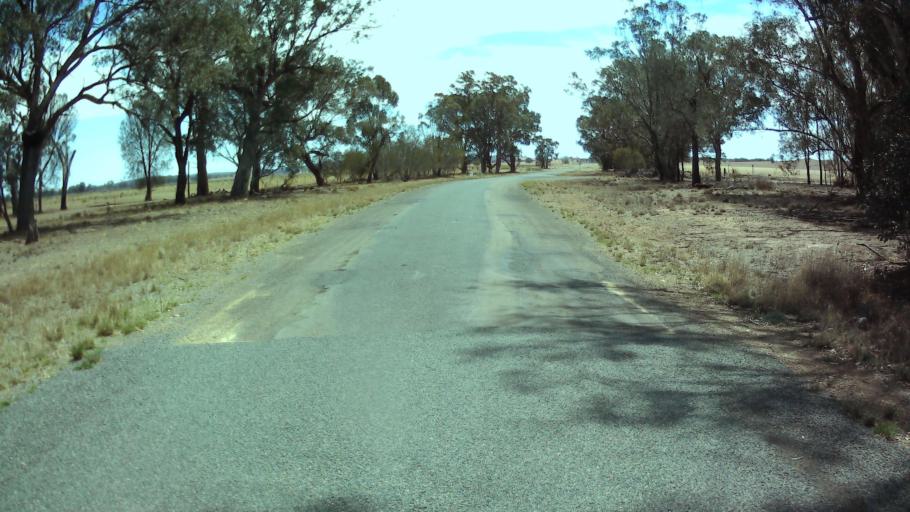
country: AU
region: New South Wales
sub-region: Weddin
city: Grenfell
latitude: -33.6421
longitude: 148.1898
